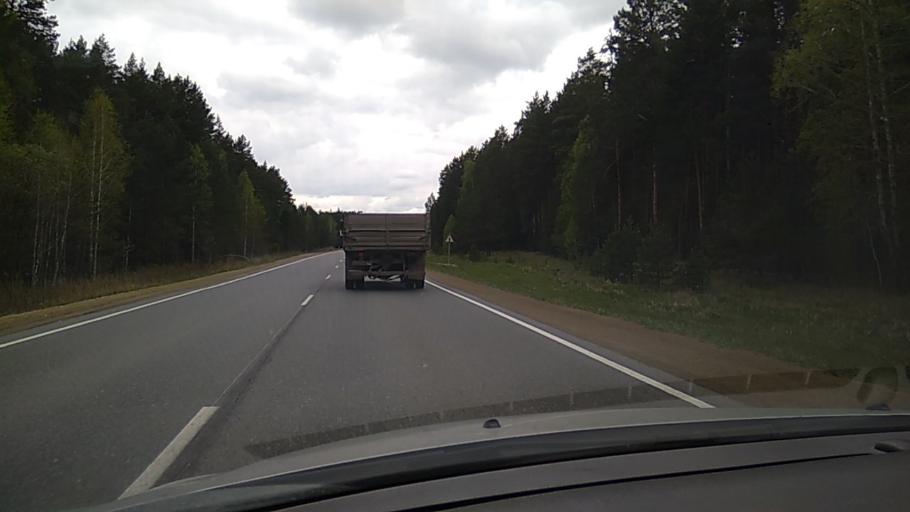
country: RU
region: Kurgan
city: Kataysk
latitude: 56.3001
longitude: 62.3751
